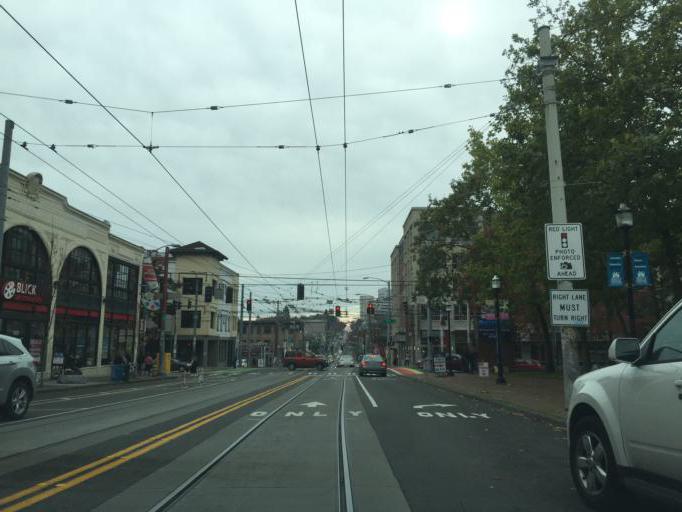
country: US
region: Washington
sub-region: King County
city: Seattle
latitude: 47.6158
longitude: -122.3209
